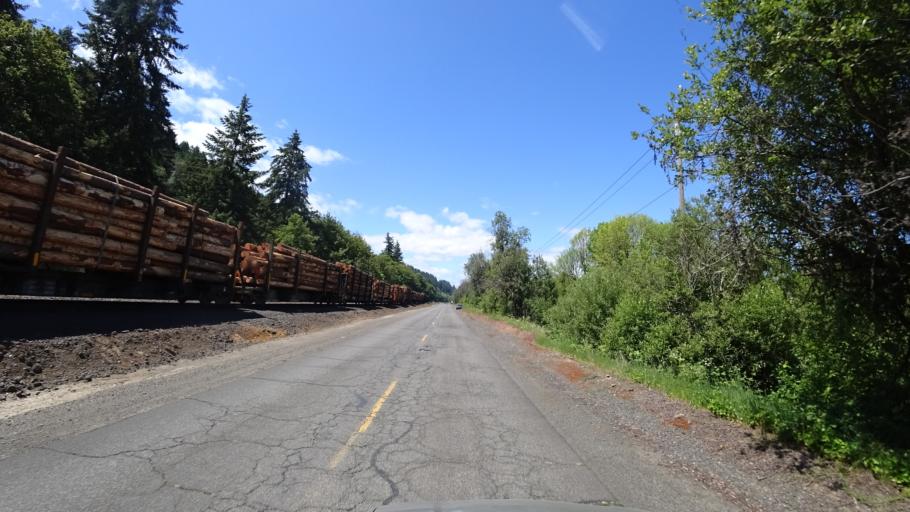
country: US
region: Oregon
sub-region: Washington County
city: Oak Hills
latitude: 45.6148
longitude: -122.8009
